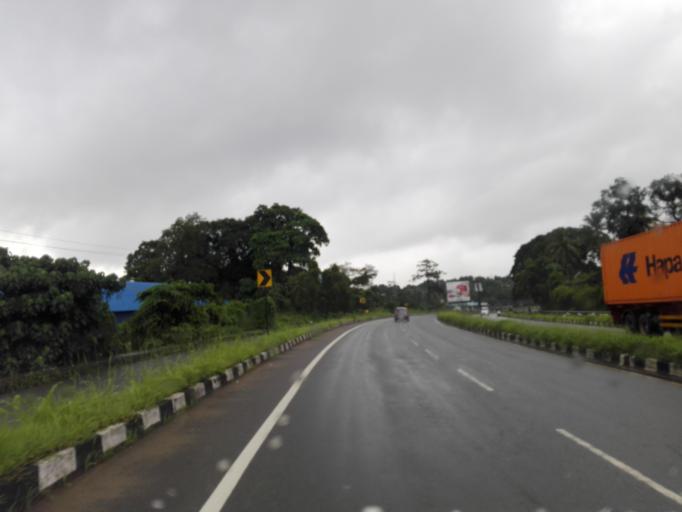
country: IN
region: Kerala
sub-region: Ernakulam
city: Elur
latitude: 10.0711
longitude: 76.3183
